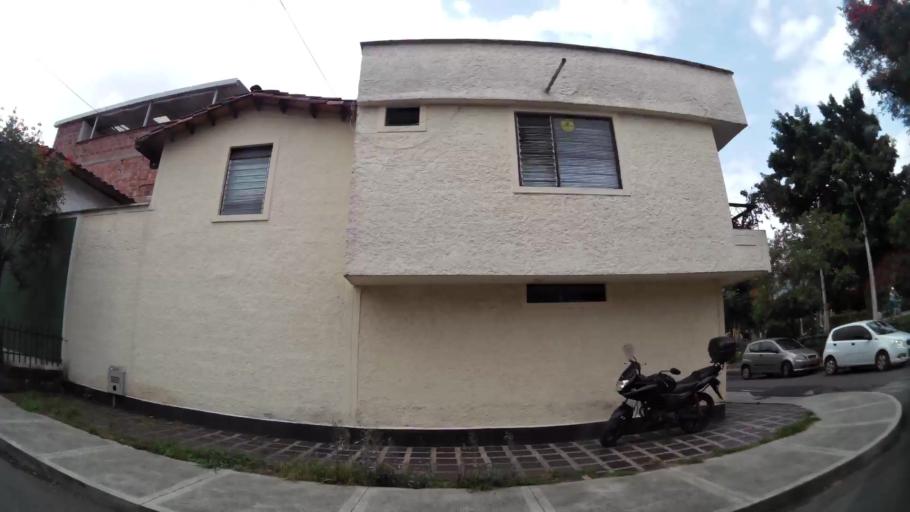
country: CO
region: Antioquia
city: Itagui
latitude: 6.2104
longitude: -75.5860
